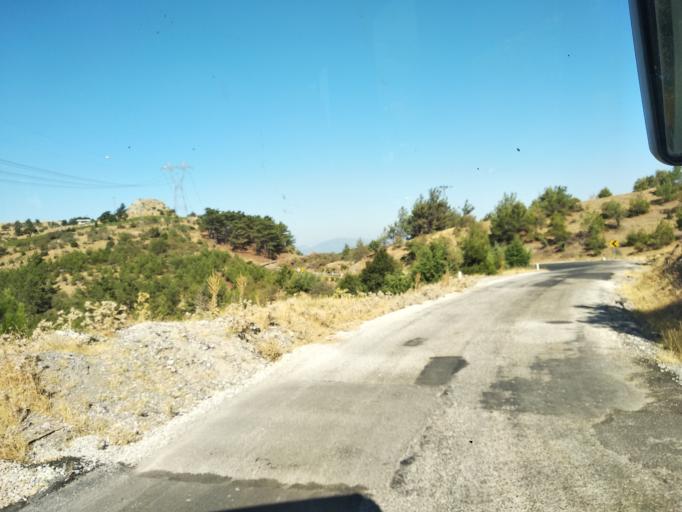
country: TR
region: Izmir
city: Gaziemir
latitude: 38.3124
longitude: 27.0010
